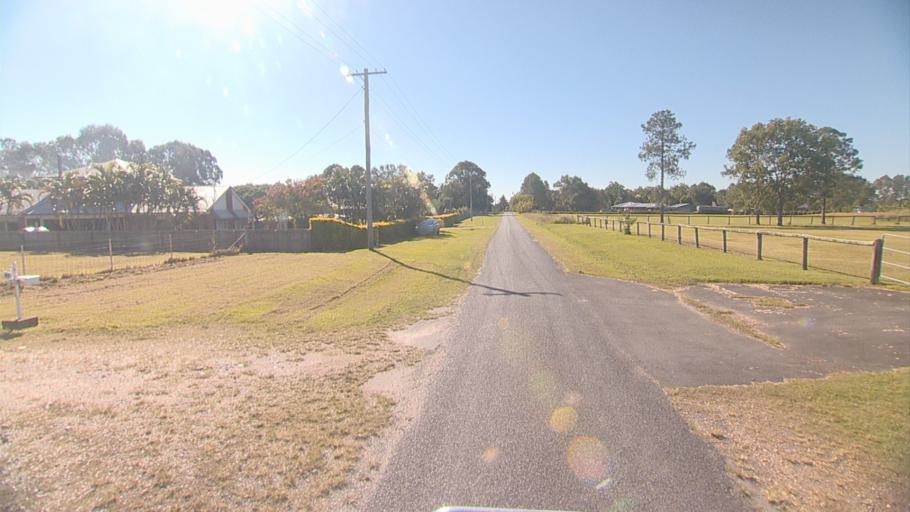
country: AU
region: Queensland
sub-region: Logan
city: Waterford West
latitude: -27.7182
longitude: 153.1261
